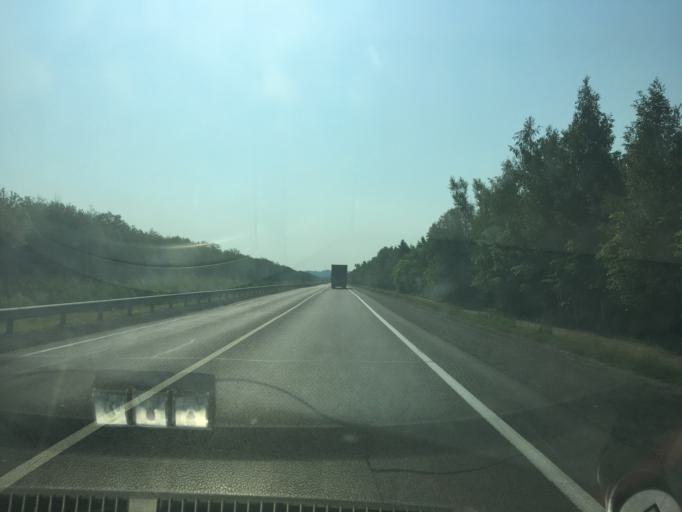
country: RU
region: Nizjnij Novgorod
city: Kstovo
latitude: 56.0883
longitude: 44.3383
